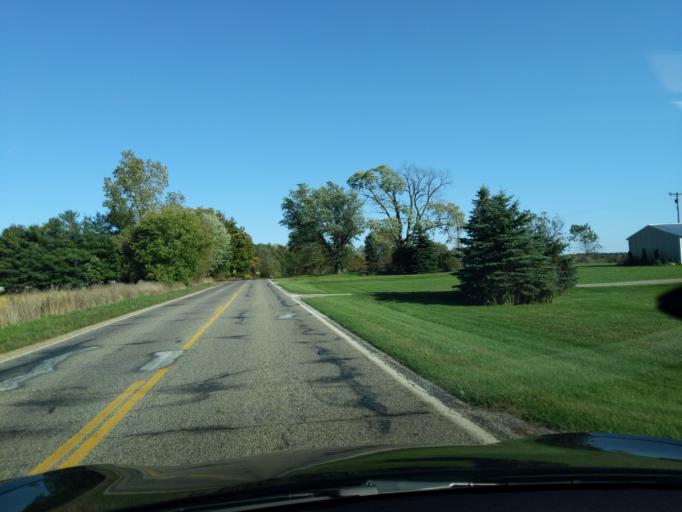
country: US
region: Michigan
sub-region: Clinton County
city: Saint Johns
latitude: 42.9289
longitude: -84.4805
